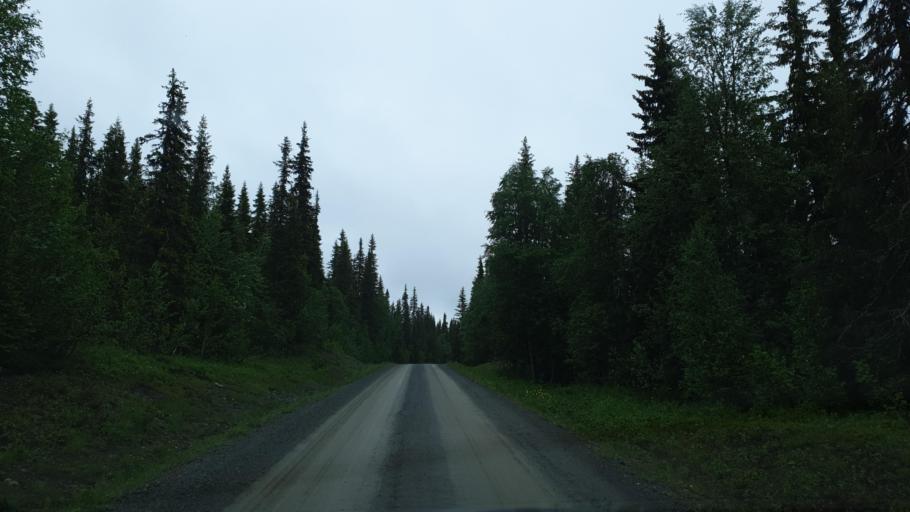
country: SE
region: Vaesterbotten
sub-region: Vilhelmina Kommun
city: Sjoberg
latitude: 65.3395
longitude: 15.8889
